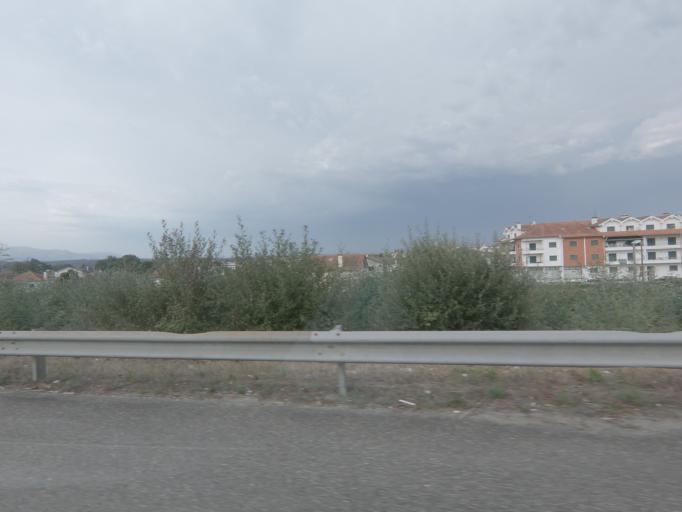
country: PT
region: Viseu
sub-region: Concelho de Tondela
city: Tondela
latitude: 40.5126
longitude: -8.0891
